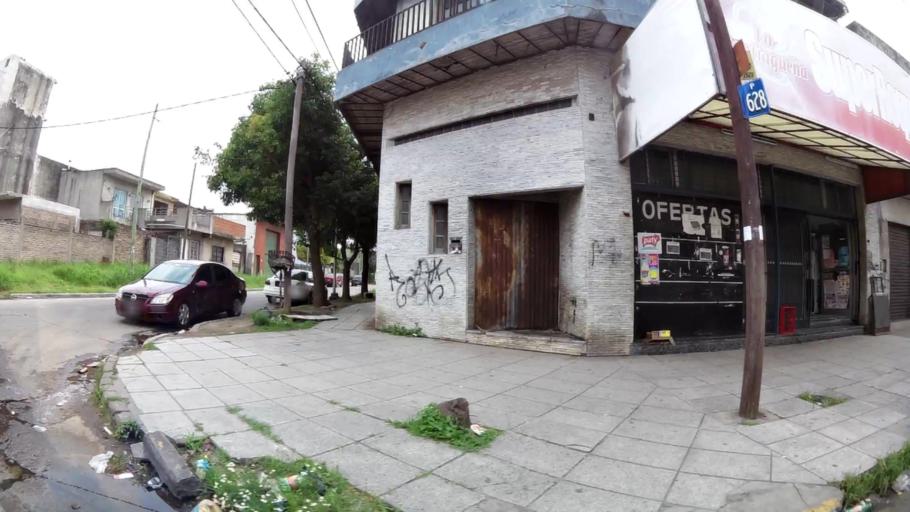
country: AR
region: Buenos Aires
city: San Justo
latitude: -34.6983
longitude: -58.5281
